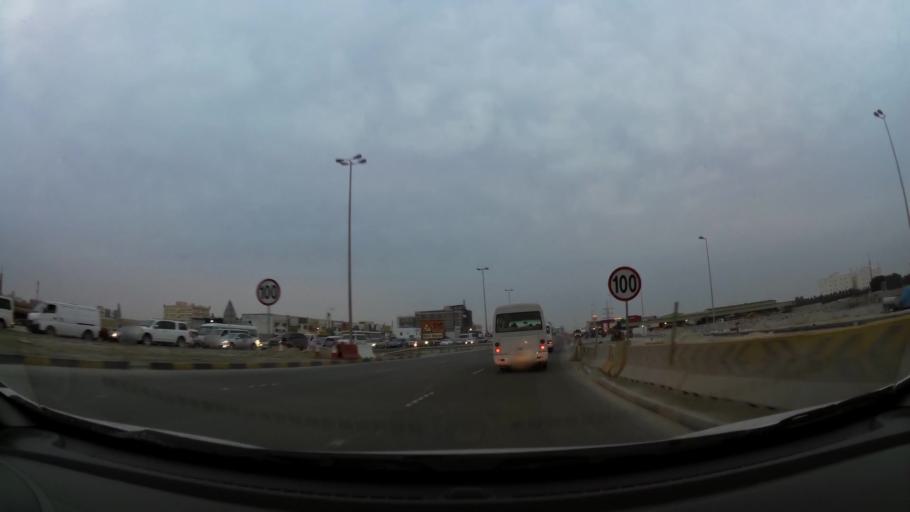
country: BH
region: Northern
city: Ar Rifa'
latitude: 26.1245
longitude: 50.5909
